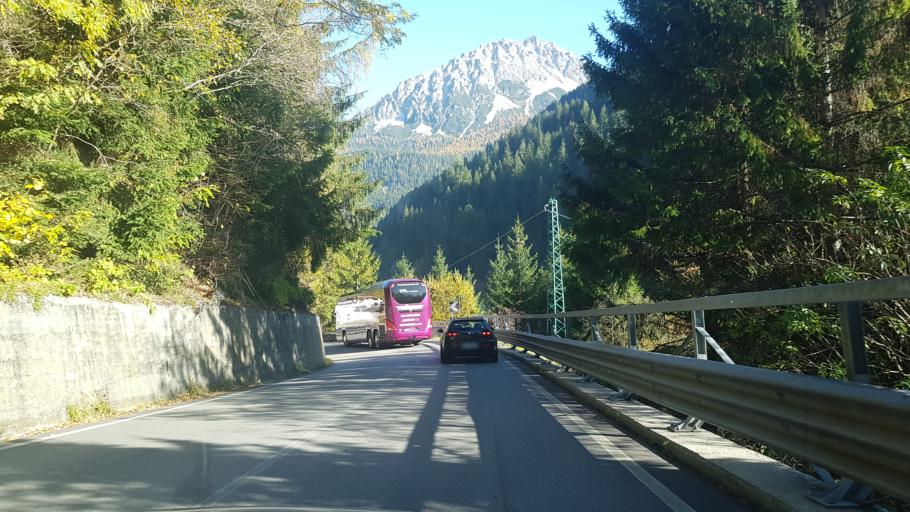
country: IT
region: Veneto
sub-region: Provincia di Belluno
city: Candide
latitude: 46.6006
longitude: 12.5228
